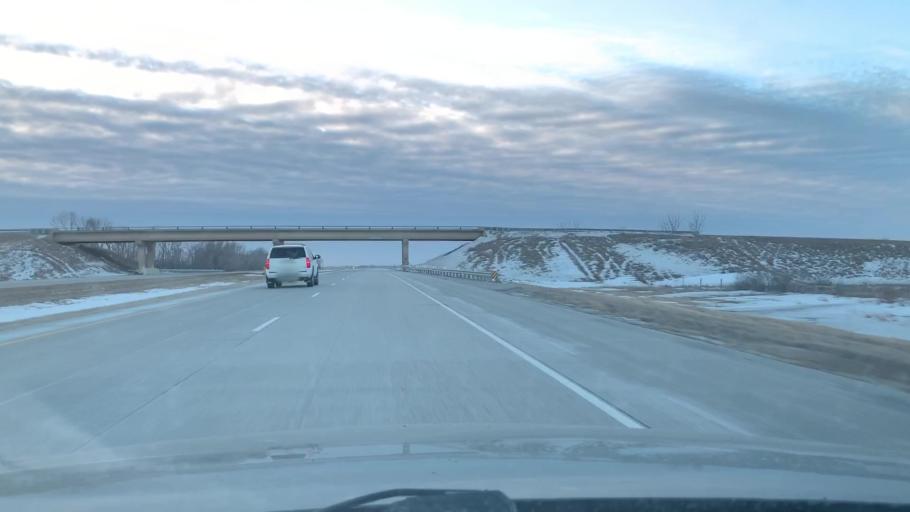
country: US
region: North Dakota
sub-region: Ransom County
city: Sheldon
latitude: 46.8760
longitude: -97.5966
